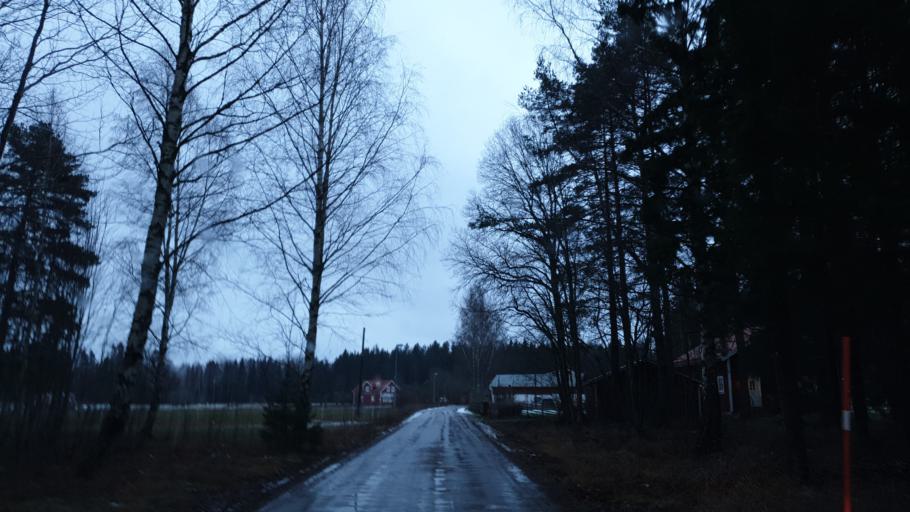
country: SE
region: Uppsala
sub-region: Tierps Kommun
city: Tierp
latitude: 60.3411
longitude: 17.4743
